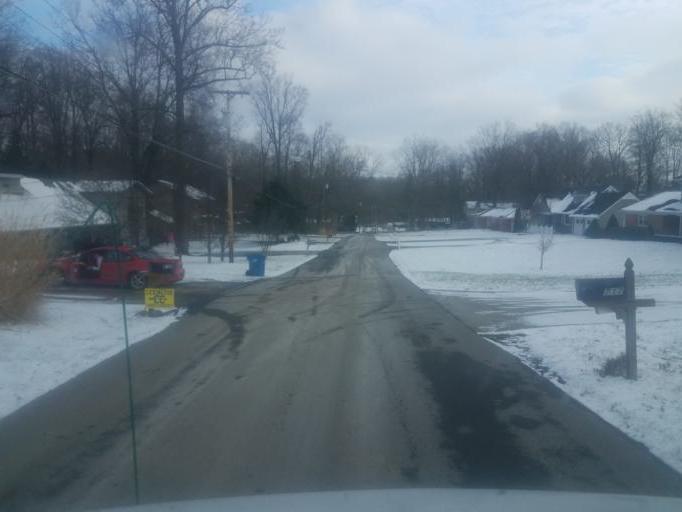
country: US
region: Ohio
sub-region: Richland County
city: Mansfield
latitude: 40.7185
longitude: -82.5424
